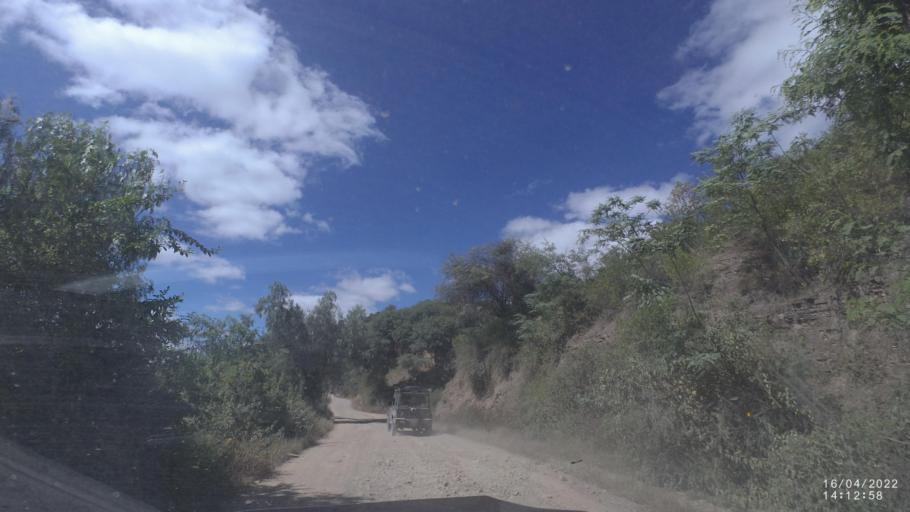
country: BO
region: Cochabamba
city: Mizque
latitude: -18.0611
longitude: -65.5110
